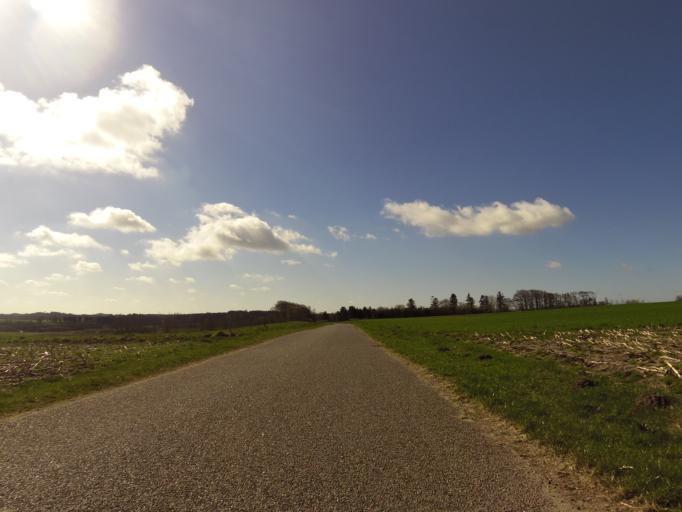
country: DK
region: Central Jutland
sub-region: Holstebro Kommune
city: Vinderup
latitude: 56.4315
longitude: 8.7323
